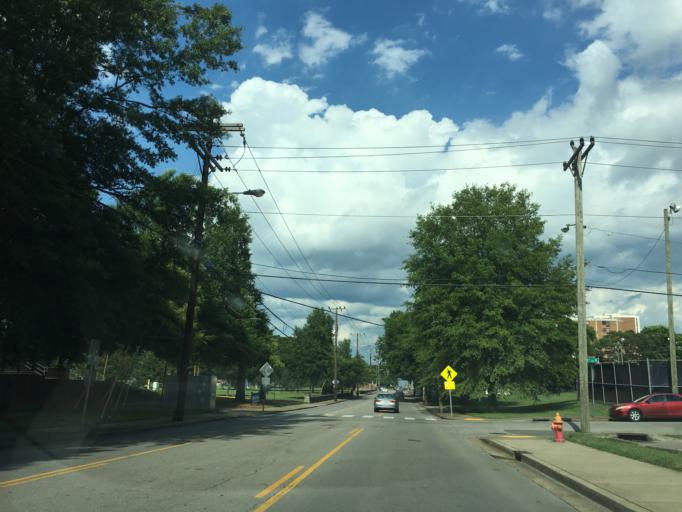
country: US
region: Tennessee
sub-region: Davidson County
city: Nashville
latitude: 36.1675
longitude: -86.8248
